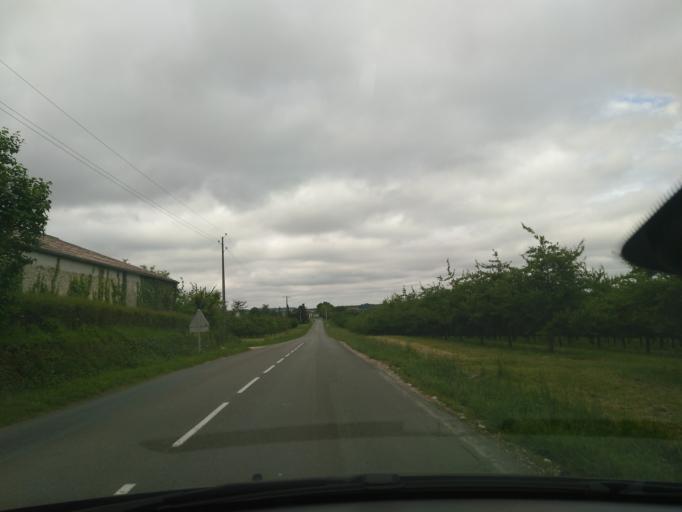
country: FR
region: Aquitaine
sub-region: Departement du Lot-et-Garonne
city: Cancon
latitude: 44.5399
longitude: 0.6091
